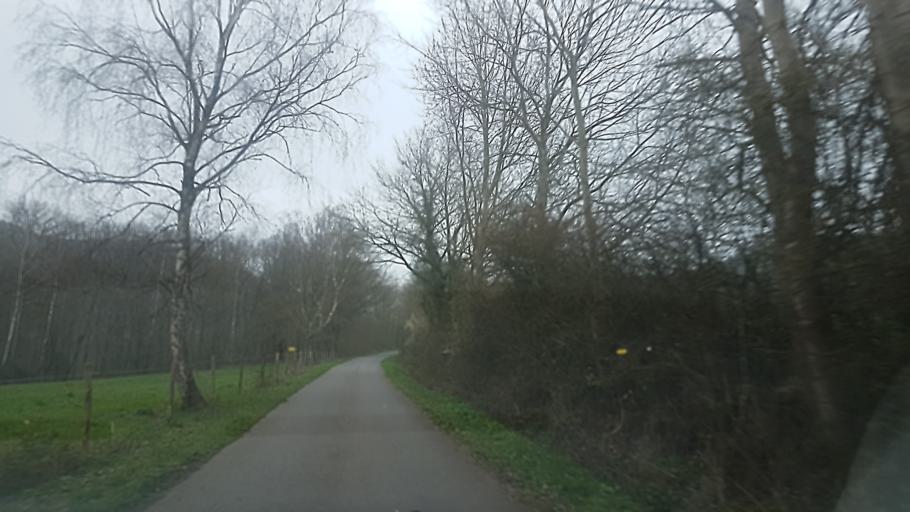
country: FR
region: Champagne-Ardenne
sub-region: Departement des Ardennes
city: Vireux-Molhain
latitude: 50.0780
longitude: 4.6469
